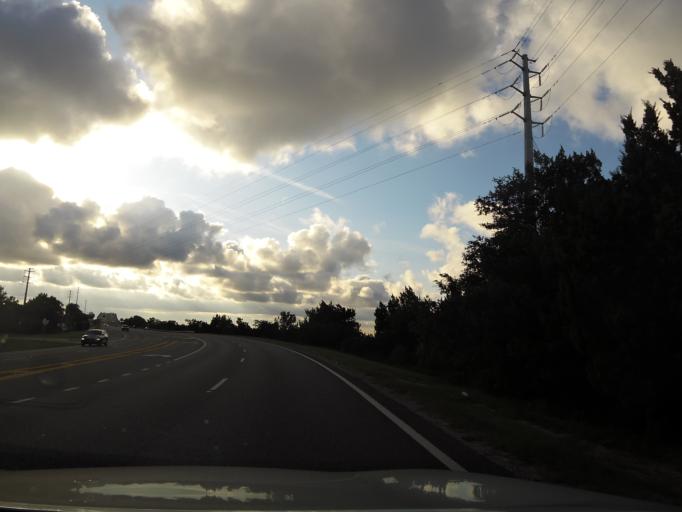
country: US
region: Georgia
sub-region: Glynn County
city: Saint Simon Mills
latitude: 31.1693
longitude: -81.4156
